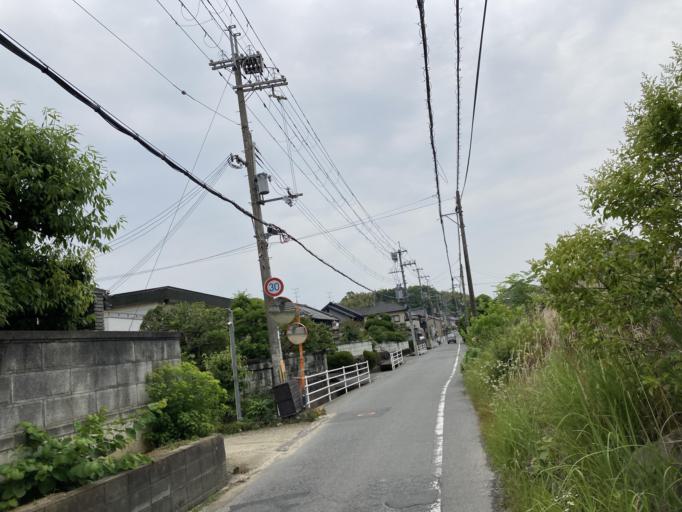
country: JP
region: Osaka
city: Kashihara
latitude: 34.5631
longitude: 135.7026
